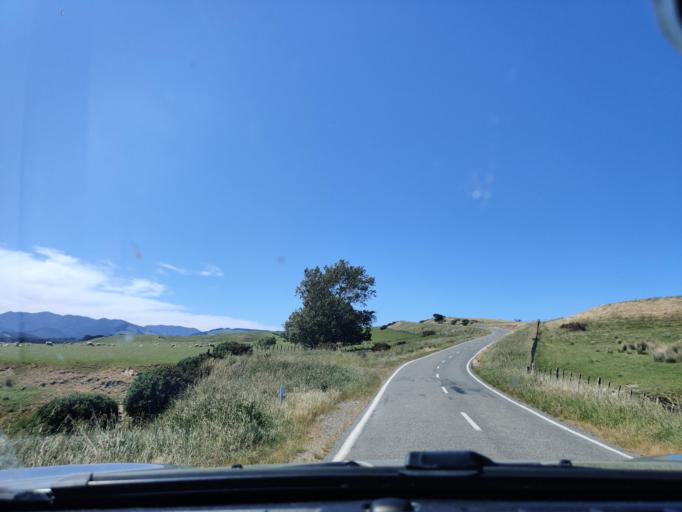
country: NZ
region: Wellington
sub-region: Upper Hutt City
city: Upper Hutt
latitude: -41.3745
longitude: 175.1777
